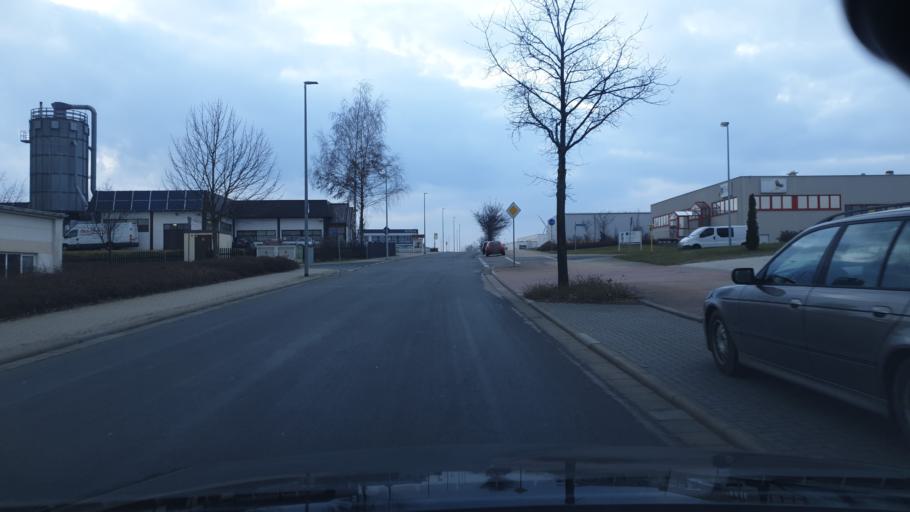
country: DE
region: Saxony
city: Mittweida
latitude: 50.9908
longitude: 12.9556
